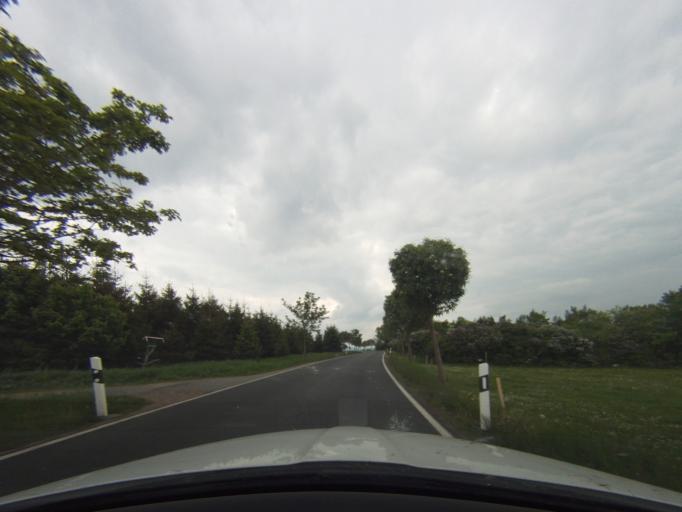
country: DE
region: Thuringia
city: Drobischau
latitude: 50.6352
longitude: 11.0762
